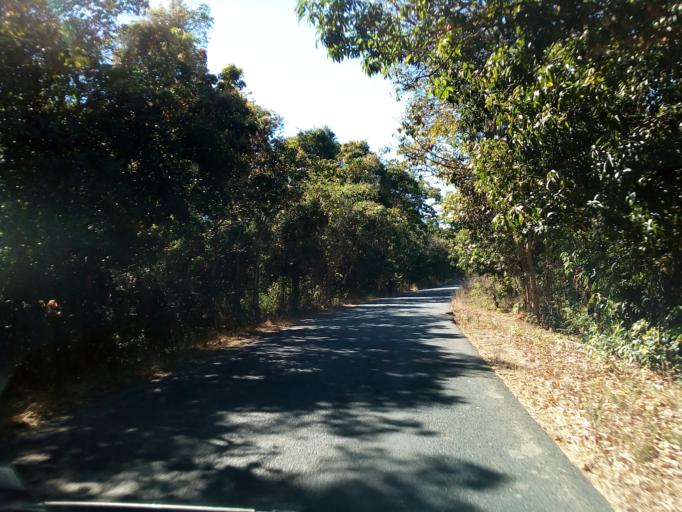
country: MG
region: Boeny
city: Marovoay
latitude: -16.2632
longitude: 46.8029
